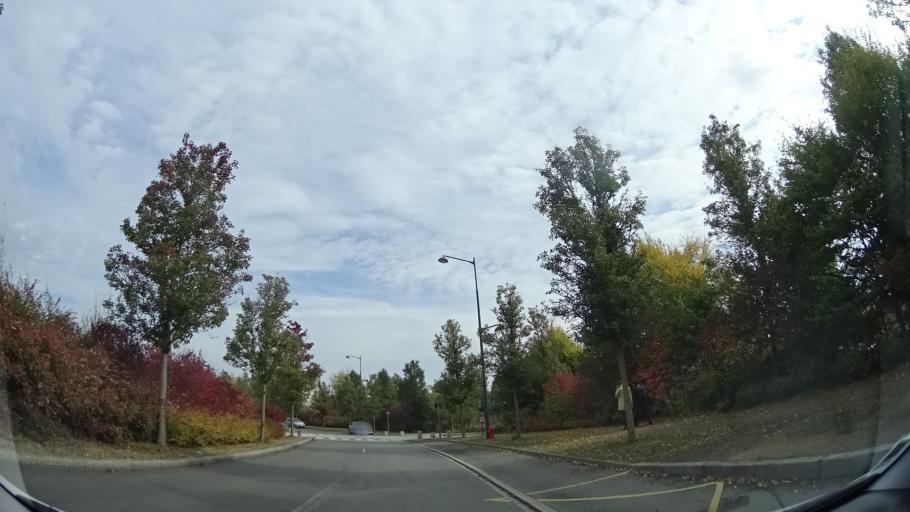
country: FR
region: Brittany
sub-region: Departement d'Ille-et-Vilaine
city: Rennes
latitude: 48.1138
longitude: -1.7127
